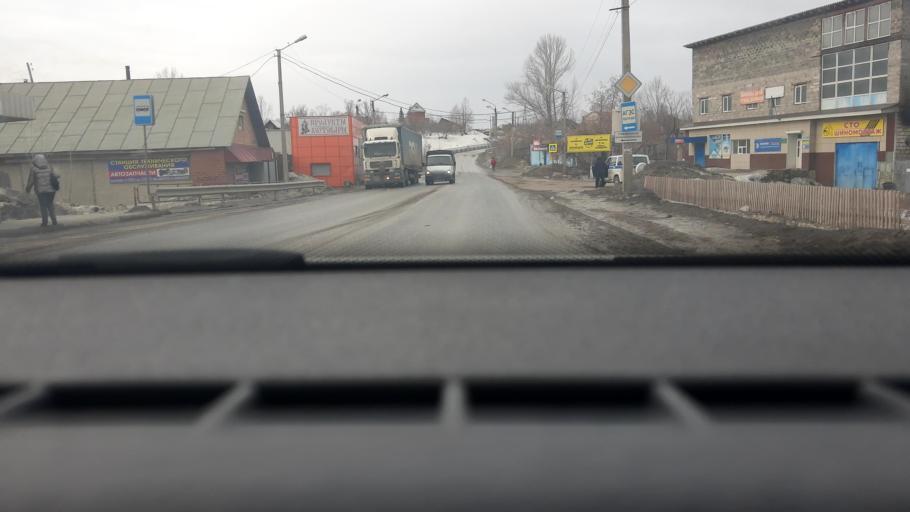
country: RU
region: Chelyabinsk
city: Asha
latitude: 54.9951
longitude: 57.2601
